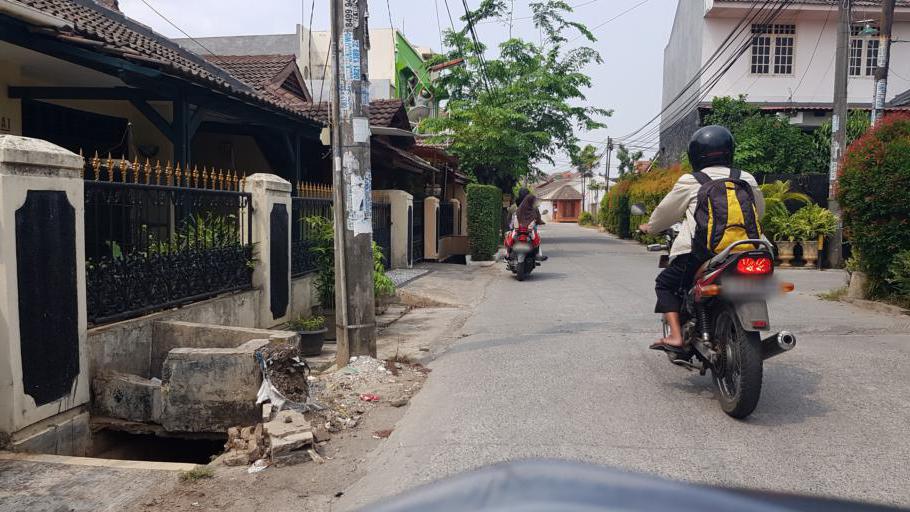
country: ID
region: West Java
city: Bekasi
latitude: -6.2798
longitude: 106.9433
